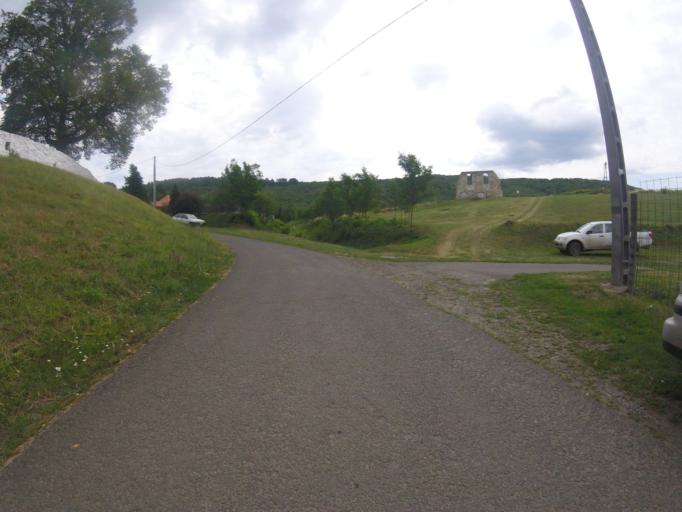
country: HU
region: Nograd
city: Tar
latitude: 47.9468
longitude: 19.7460
